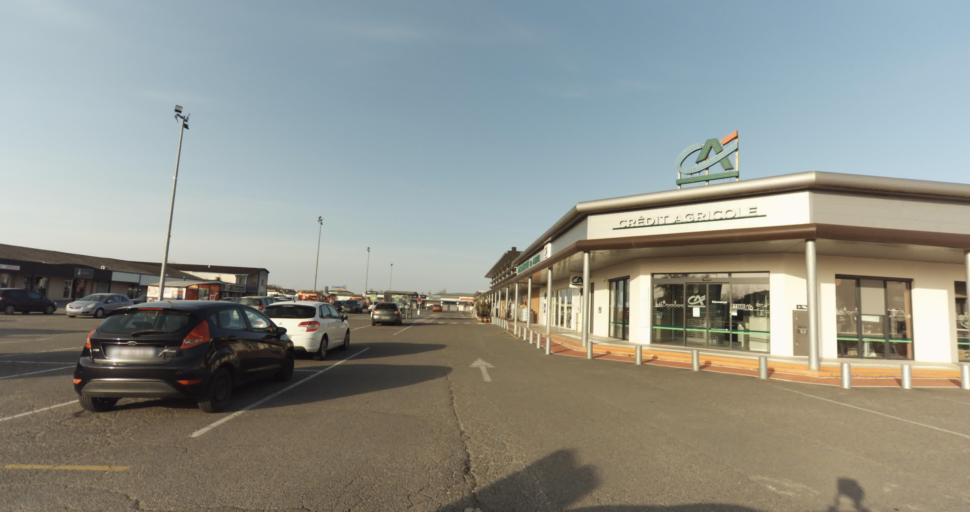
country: FR
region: Midi-Pyrenees
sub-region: Departement du Tarn
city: Saint-Sulpice-la-Pointe
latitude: 43.7726
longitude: 1.6771
